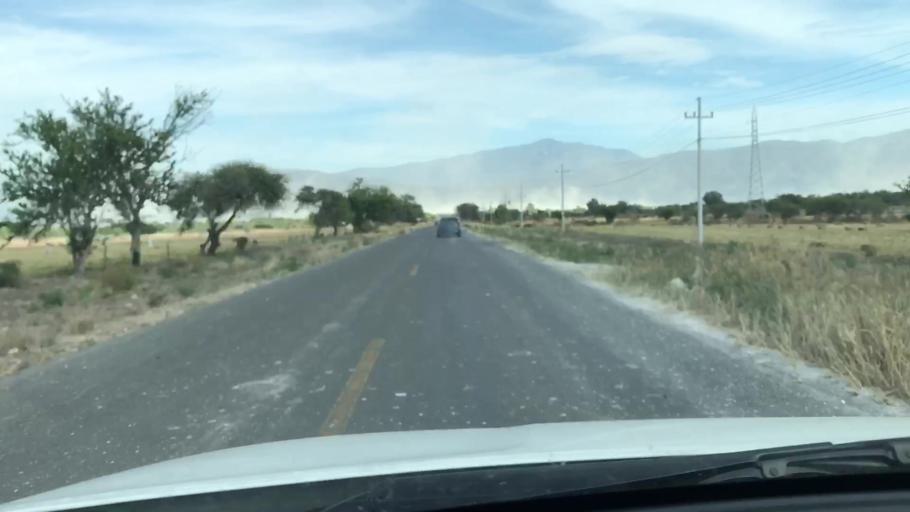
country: MX
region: Jalisco
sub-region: Zacoalco de Torres
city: Barranca de Otates (Barranca de Otatan)
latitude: 20.2855
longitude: -103.6136
